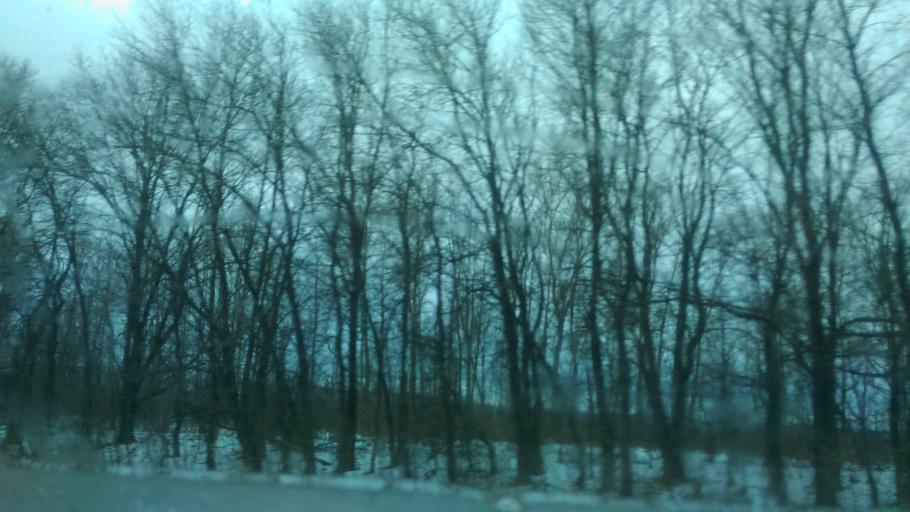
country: RU
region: Tula
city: Bolokhovo
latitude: 54.0850
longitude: 37.7768
